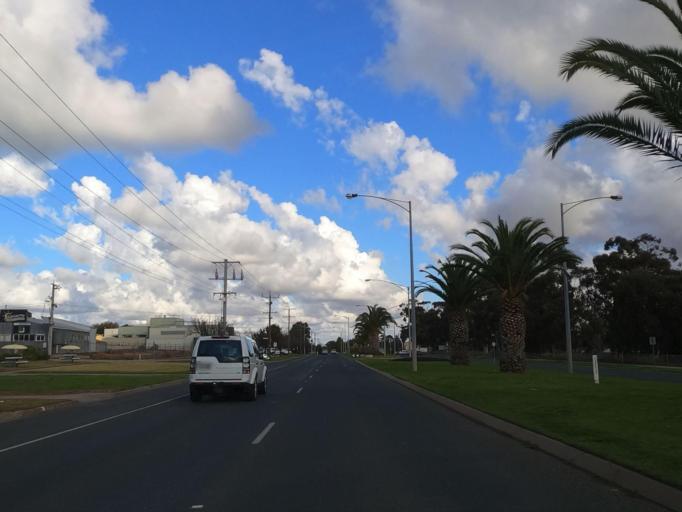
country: AU
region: Victoria
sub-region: Swan Hill
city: Swan Hill
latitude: -35.3538
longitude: 143.5622
